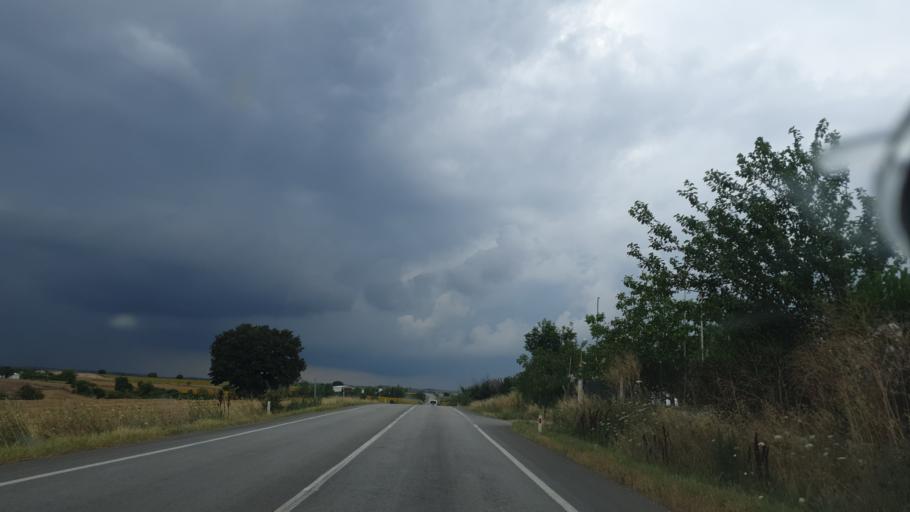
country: TR
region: Tekirdag
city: Hayrabolu
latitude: 41.2190
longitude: 27.0789
